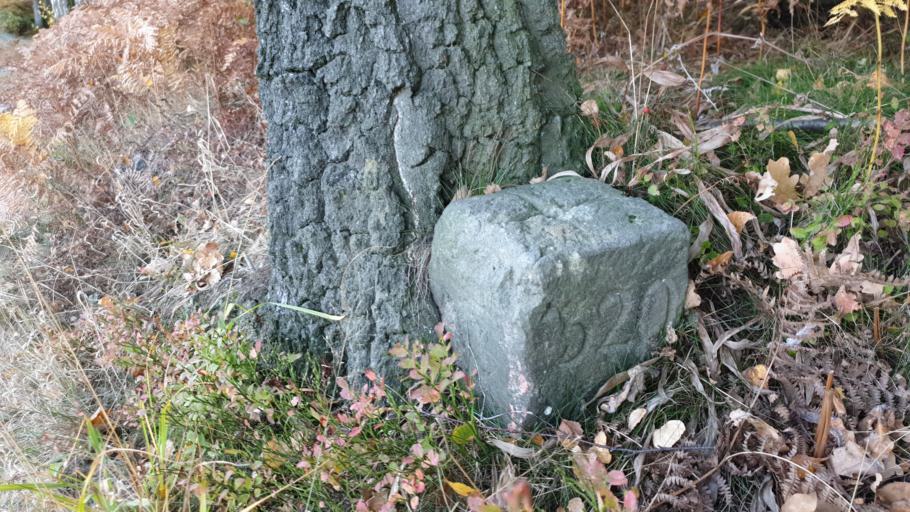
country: DE
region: Saxony
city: Bad Schandau
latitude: 50.9051
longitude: 14.1323
